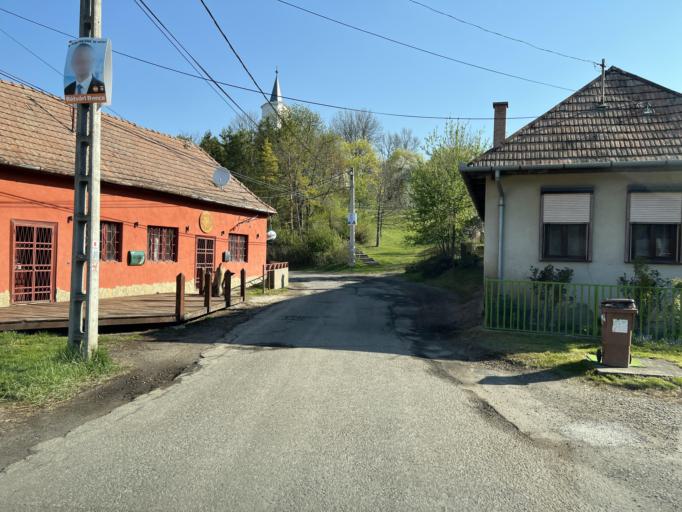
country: SK
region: Nitriansky
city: Sahy
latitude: 47.9946
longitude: 18.8629
